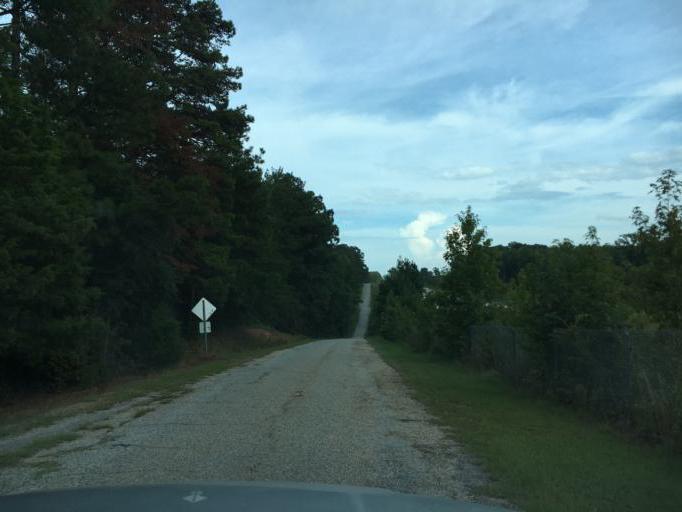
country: US
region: South Carolina
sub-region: Laurens County
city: Watts Mills
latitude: 34.5350
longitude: -81.9409
